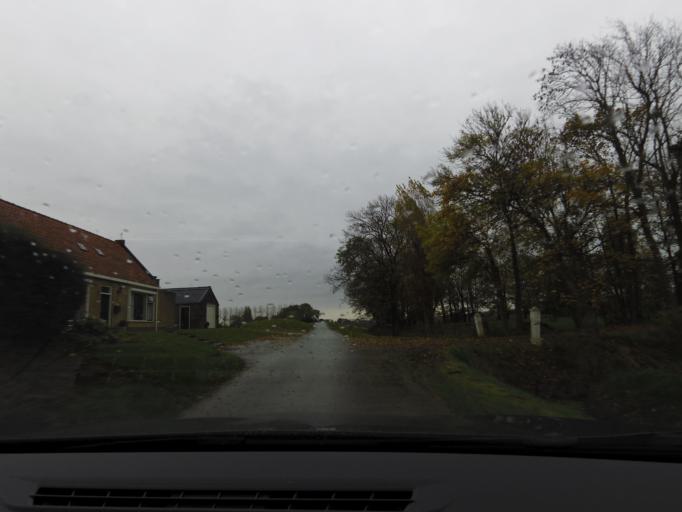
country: NL
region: South Holland
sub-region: Gemeente Goeree-Overflakkee
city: Dirksland
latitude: 51.7770
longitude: 4.0781
